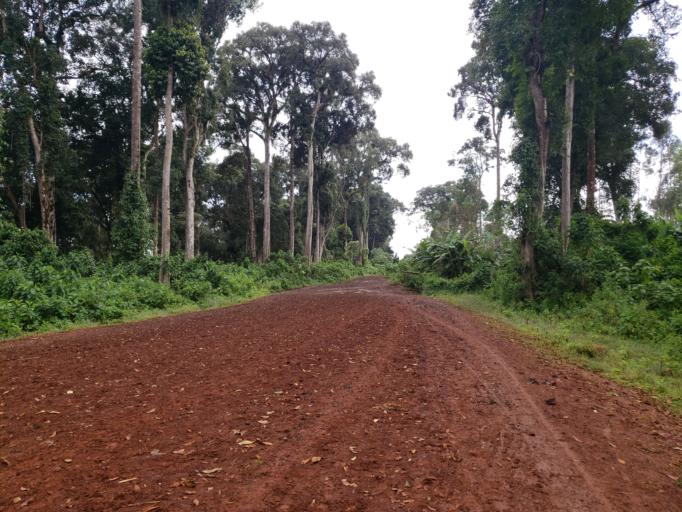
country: ET
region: Oromiya
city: Dodola
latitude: 6.5627
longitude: 39.4247
